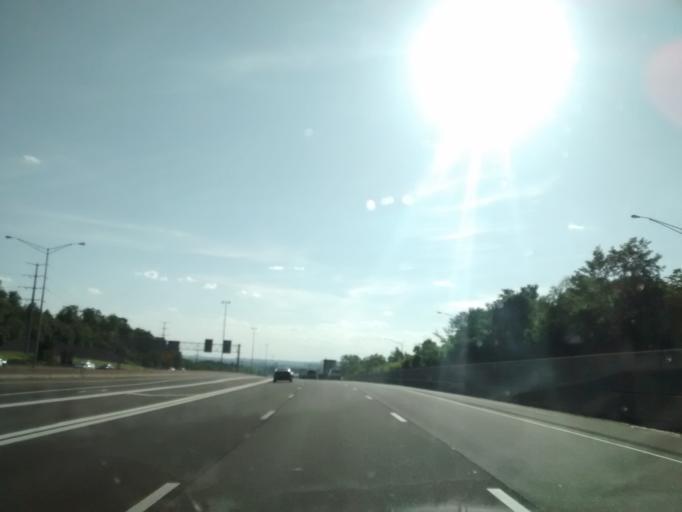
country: US
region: Connecticut
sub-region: Hartford County
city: East Hartford
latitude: 41.7735
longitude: -72.5880
